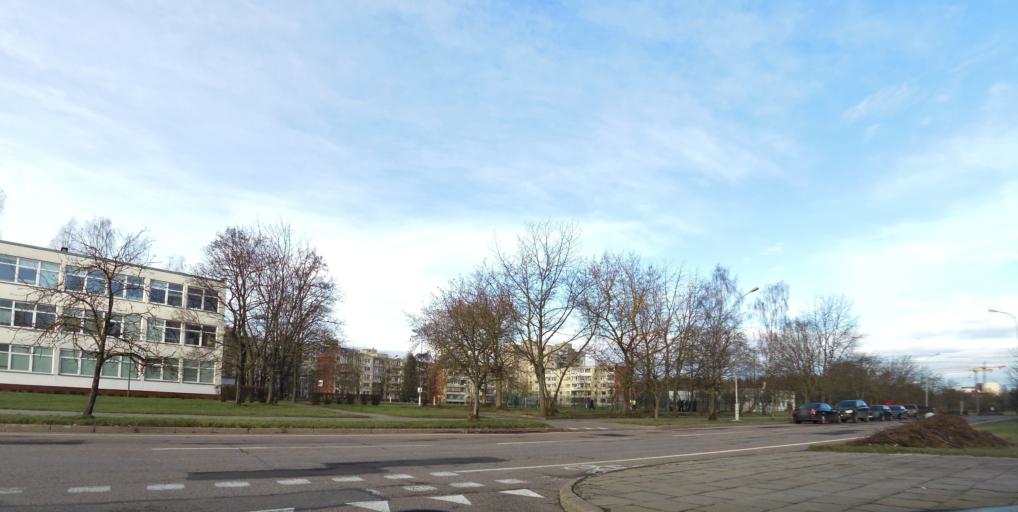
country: LT
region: Vilnius County
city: Justiniskes
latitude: 54.6969
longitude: 25.2294
